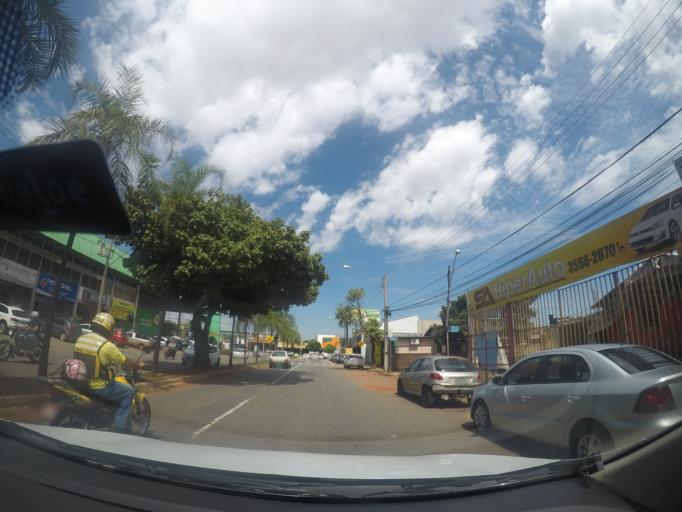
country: BR
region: Goias
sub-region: Goiania
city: Goiania
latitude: -16.6971
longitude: -49.3140
